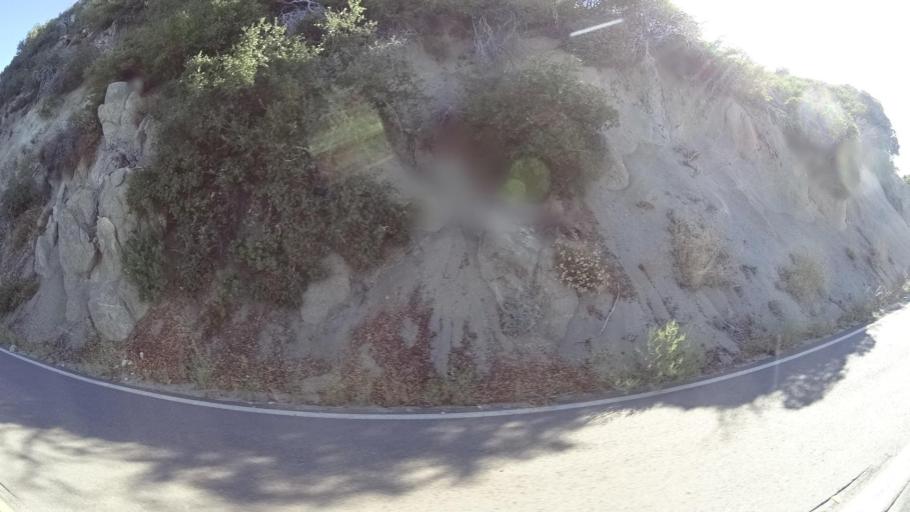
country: US
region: California
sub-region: Riverside County
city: Aguanga
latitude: 33.3064
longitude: -116.8569
